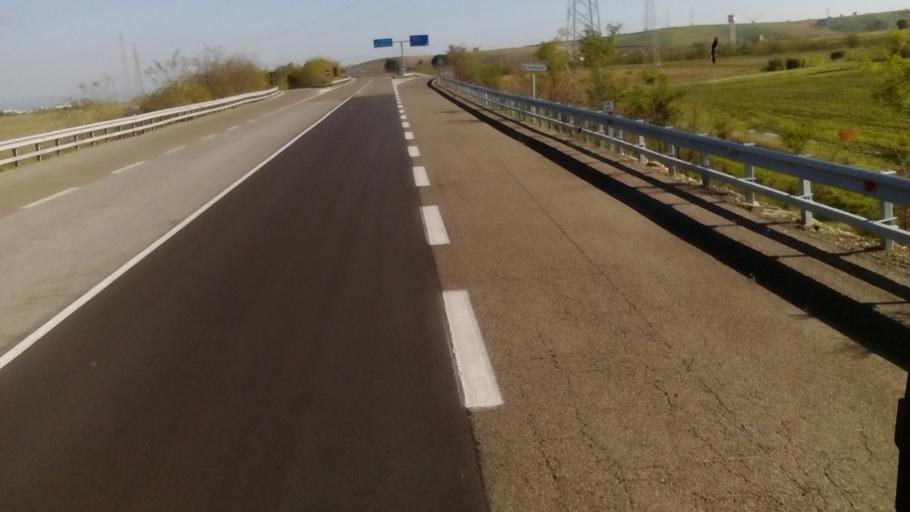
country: IT
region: Basilicate
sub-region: Provincia di Potenza
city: Melfi
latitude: 41.0654
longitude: 15.6739
